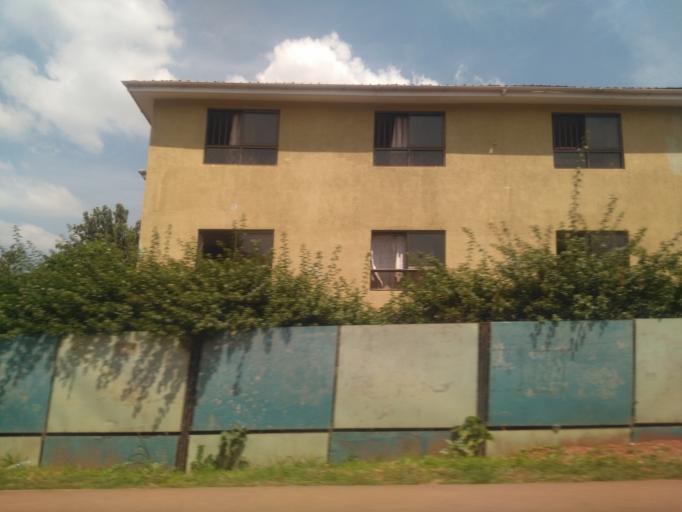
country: UG
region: Central Region
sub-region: Wakiso District
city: Entebbe
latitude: 0.0558
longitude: 32.4647
